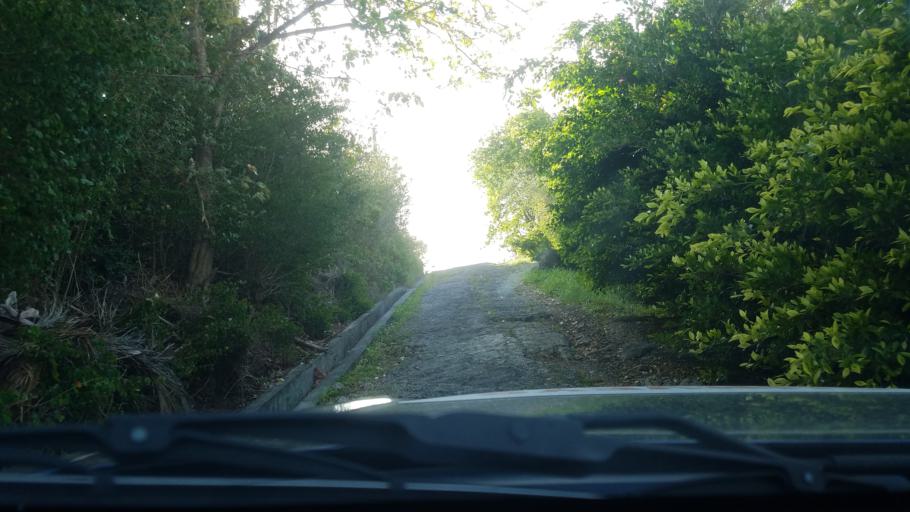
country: LC
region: Castries Quarter
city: Bisee
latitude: 14.0374
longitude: -60.9553
